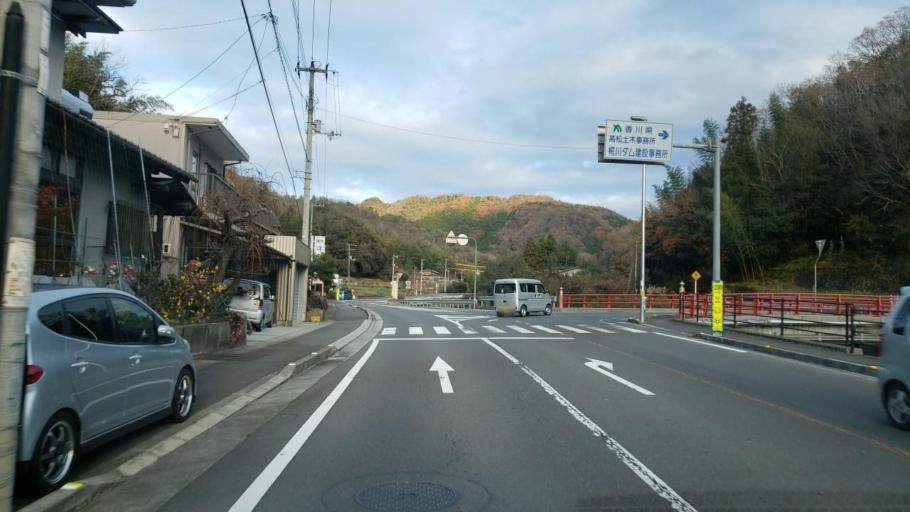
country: JP
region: Tokushima
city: Wakimachi
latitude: 34.1713
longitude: 134.0962
